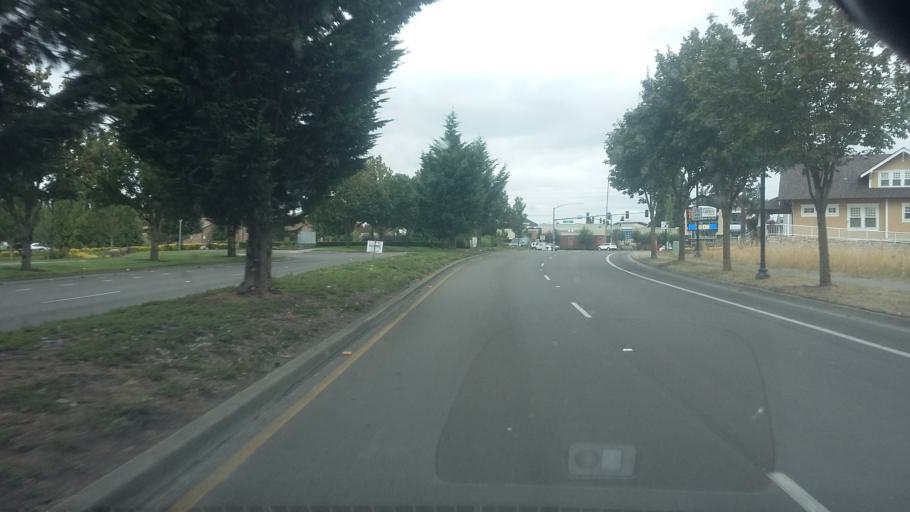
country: US
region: Washington
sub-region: Clark County
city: Mill Plain
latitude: 45.6158
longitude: -122.5020
